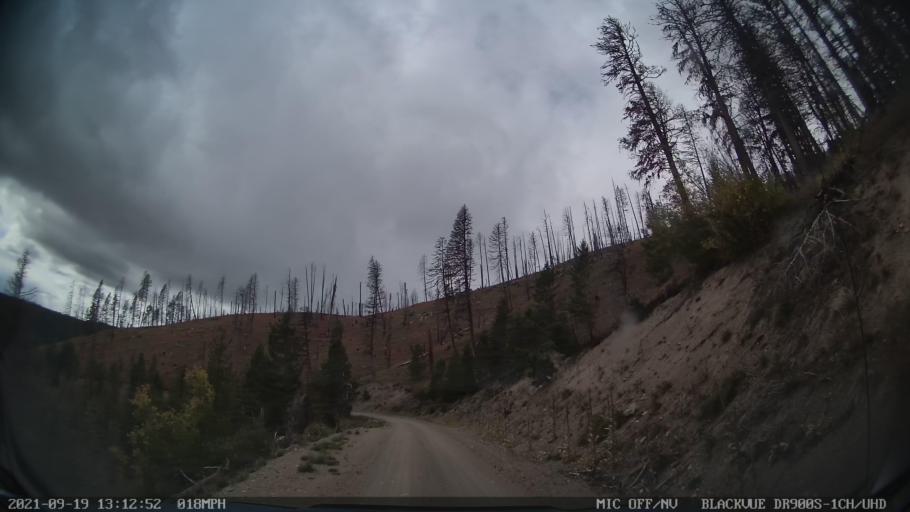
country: US
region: Montana
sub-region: Missoula County
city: Seeley Lake
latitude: 47.1781
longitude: -113.3569
